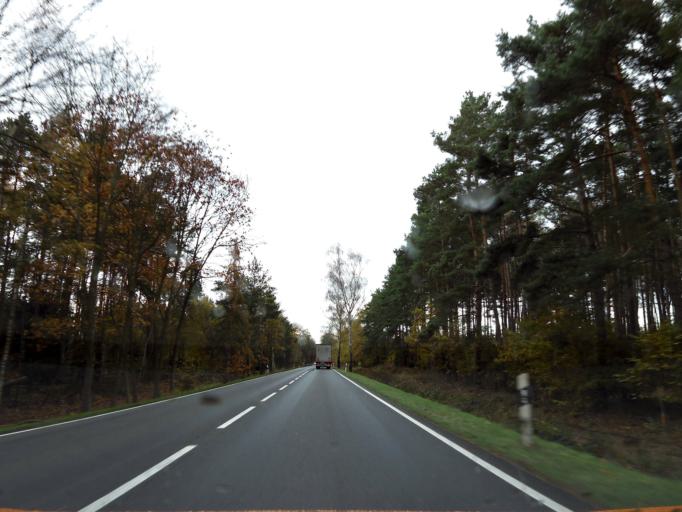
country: DE
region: Saxony-Anhalt
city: Kalbe
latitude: 52.6385
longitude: 11.3044
